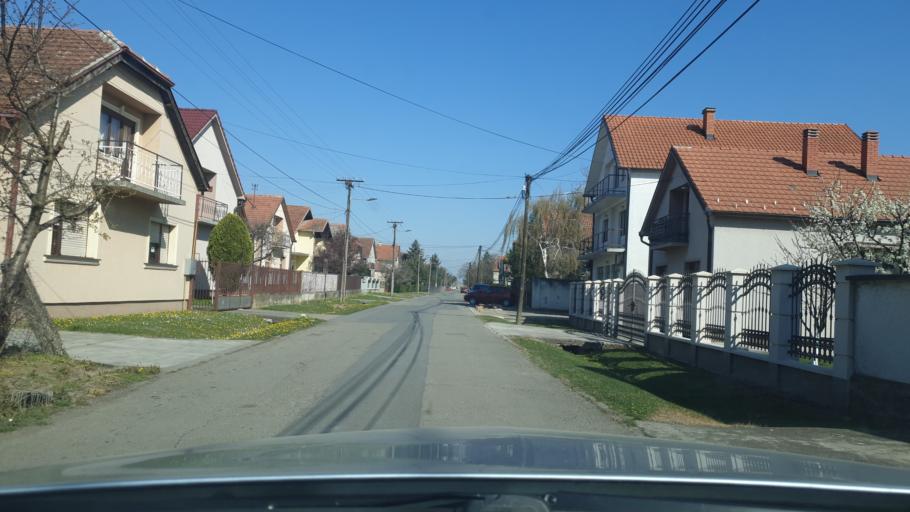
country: RS
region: Autonomna Pokrajina Vojvodina
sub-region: Sremski Okrug
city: Stara Pazova
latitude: 44.9897
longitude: 20.1432
